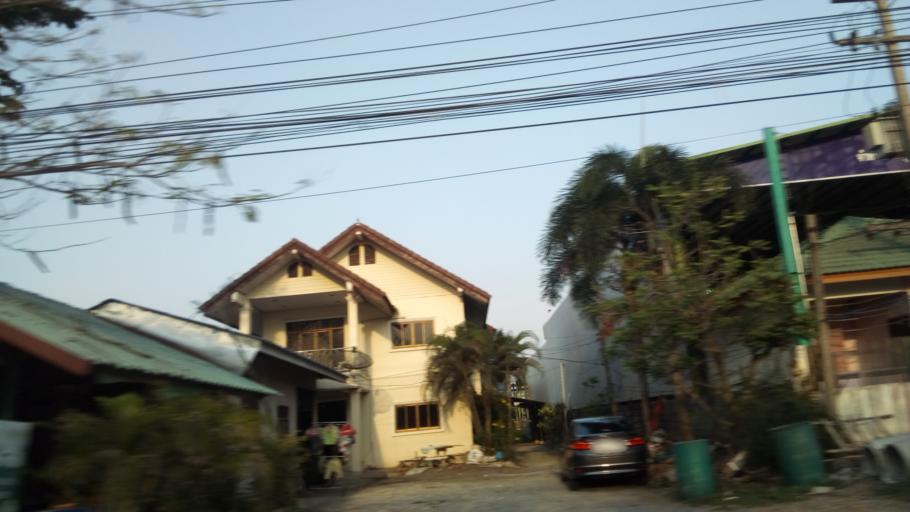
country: TH
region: Pathum Thani
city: Nong Suea
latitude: 14.1958
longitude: 100.8237
